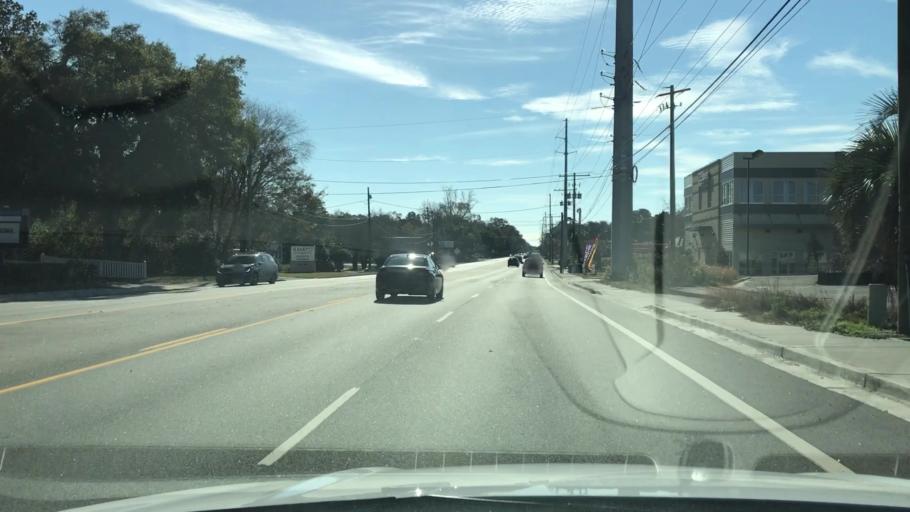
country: US
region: South Carolina
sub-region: Charleston County
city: Charleston
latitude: 32.7321
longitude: -79.9692
